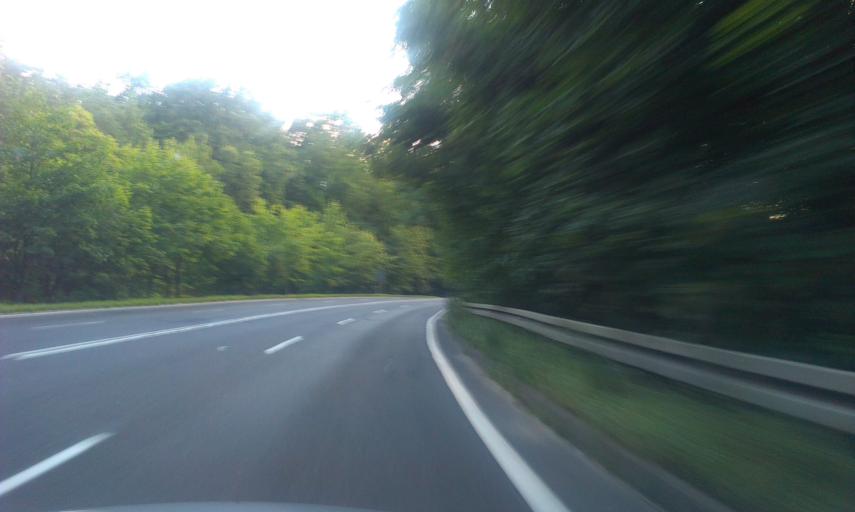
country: PL
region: West Pomeranian Voivodeship
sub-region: Koszalin
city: Koszalin
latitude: 54.2109
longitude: 16.2180
